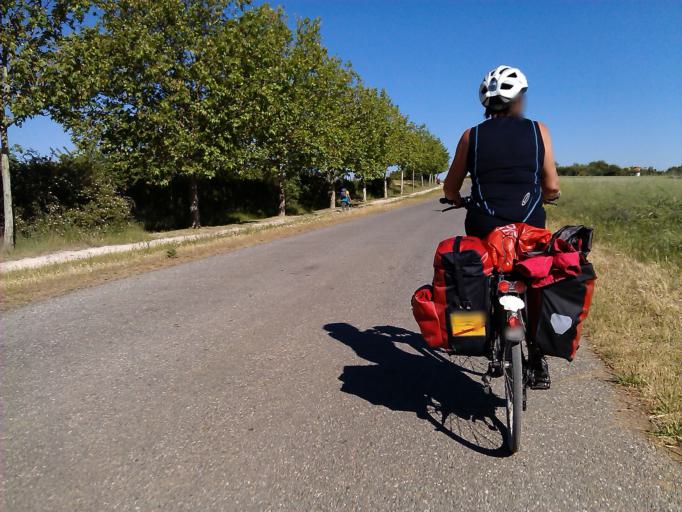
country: ES
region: Castille and Leon
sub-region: Provincia de Leon
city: Bercianos del Real Camino
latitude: 42.3898
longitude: -5.1478
